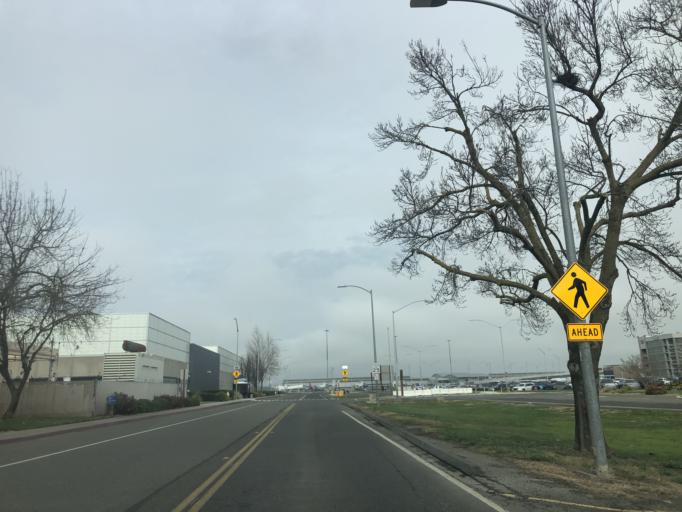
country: US
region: California
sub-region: Yolo County
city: West Sacramento
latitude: 38.6896
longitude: -121.5947
